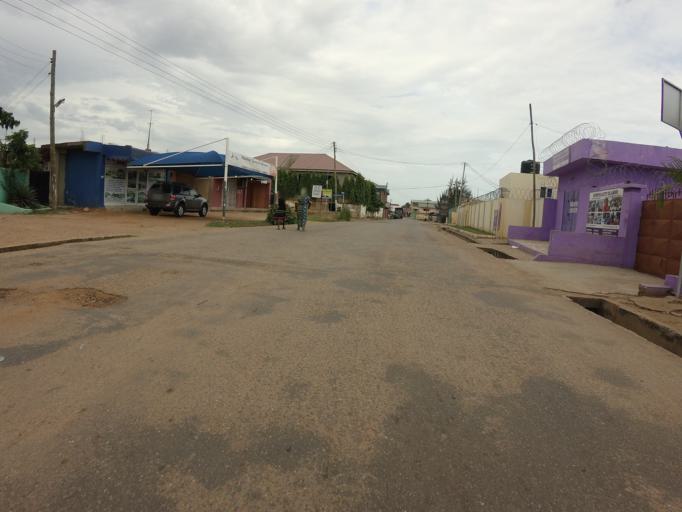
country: GH
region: Greater Accra
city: Accra
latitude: 5.6004
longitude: -0.2182
